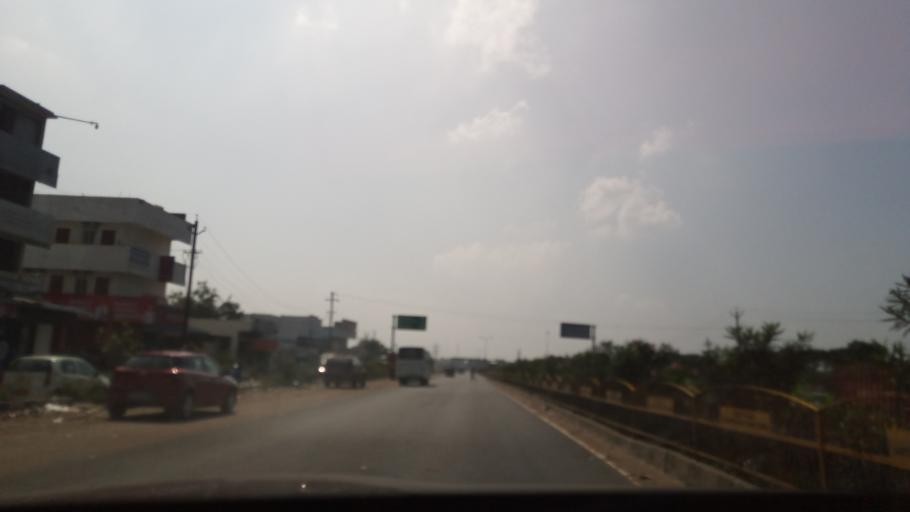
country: IN
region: Tamil Nadu
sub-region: Kancheepuram
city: Madambakkam
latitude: 12.8502
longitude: 79.9431
